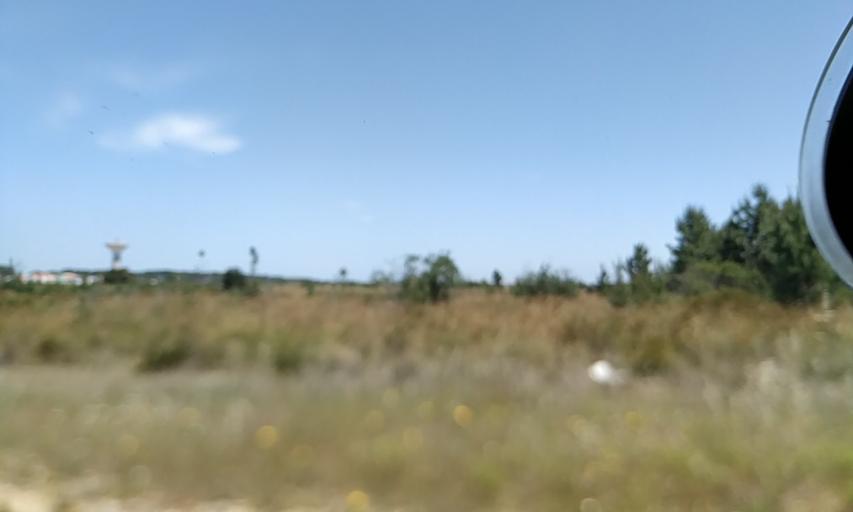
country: PT
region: Setubal
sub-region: Palmela
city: Palmela
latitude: 38.6269
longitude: -8.7466
